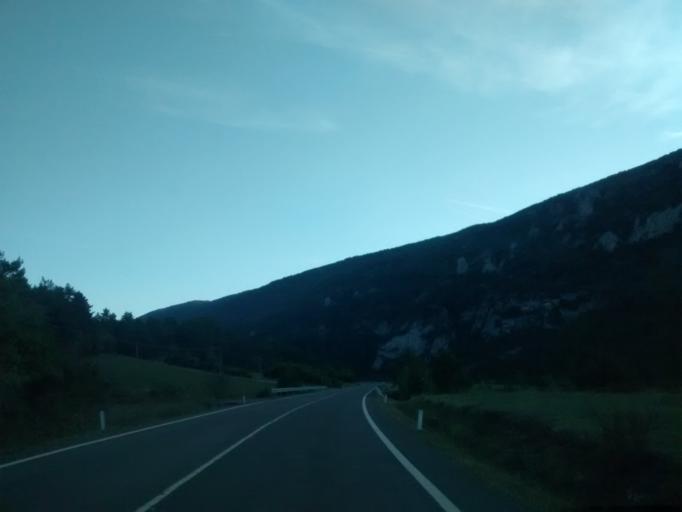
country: ES
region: Aragon
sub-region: Provincia de Huesca
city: Aragues del Puerto
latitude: 42.7122
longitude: -0.7496
